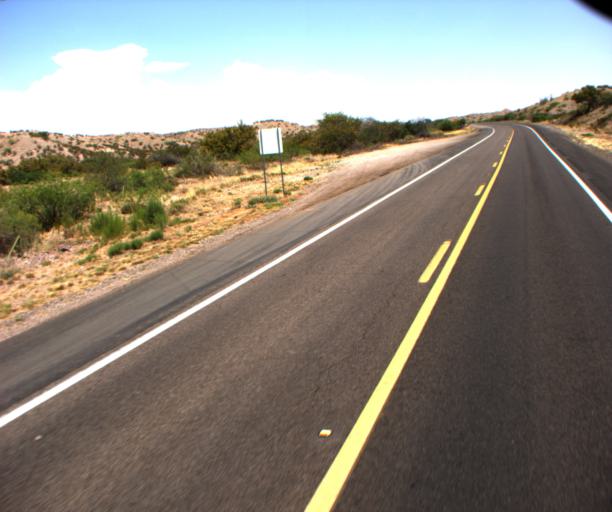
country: US
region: New Mexico
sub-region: Hidalgo County
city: Lordsburg
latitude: 32.6480
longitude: -109.0494
